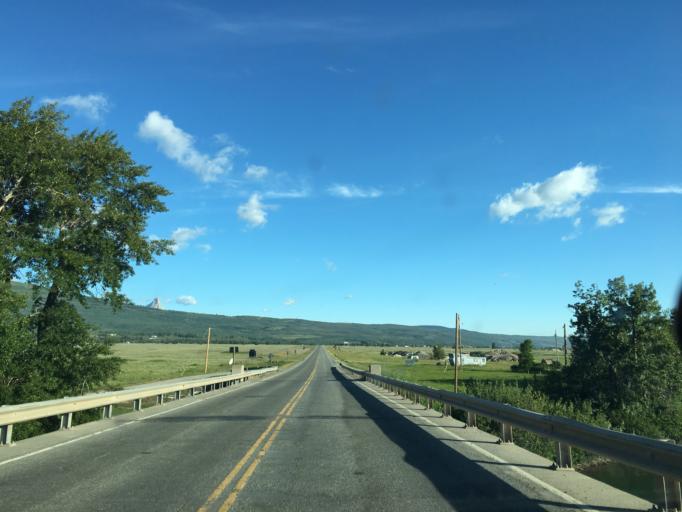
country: CA
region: Alberta
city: Cardston
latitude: 48.8438
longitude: -113.4177
